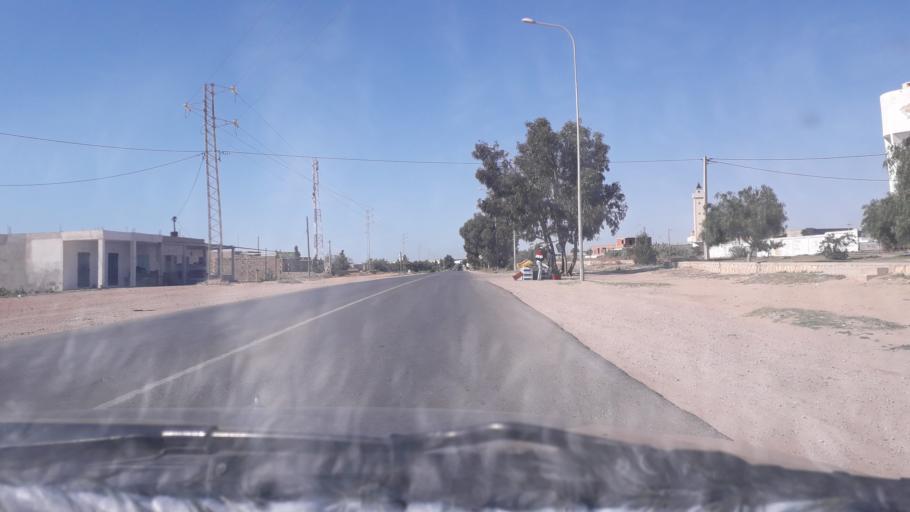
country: TN
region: Safaqis
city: Al Qarmadah
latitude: 34.8855
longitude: 10.7619
